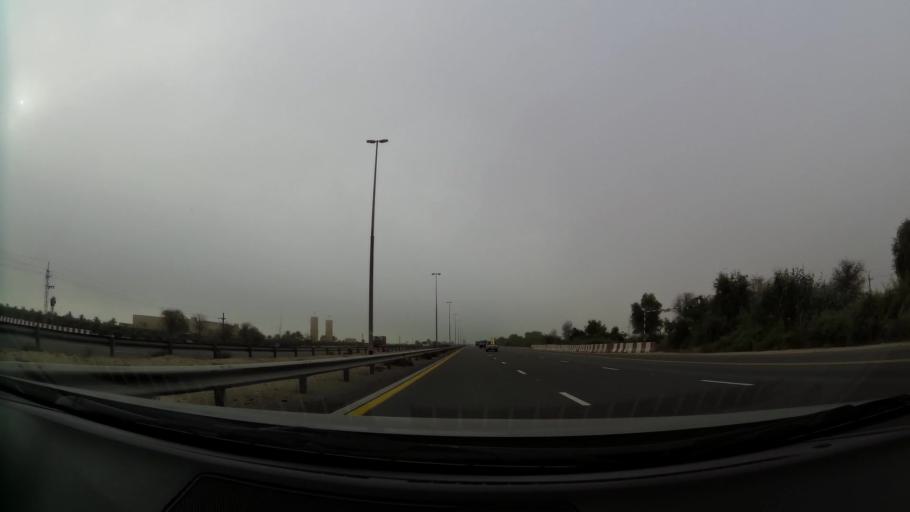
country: AE
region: Dubai
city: Dubai
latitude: 25.0709
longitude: 55.4060
